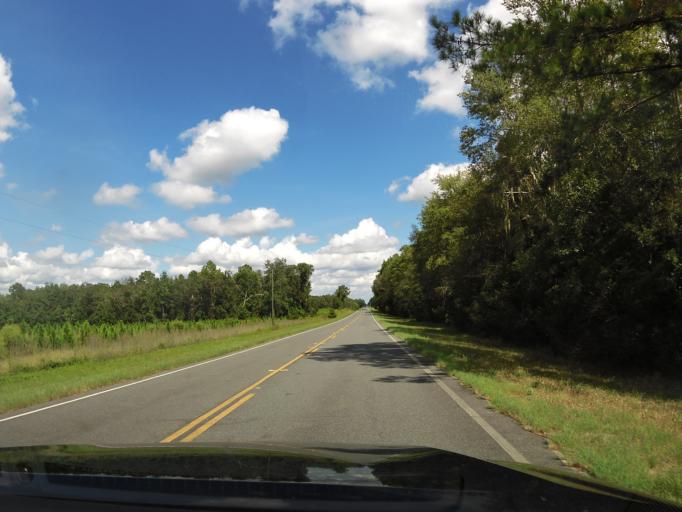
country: US
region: Florida
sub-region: Hamilton County
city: Jasper
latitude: 30.6153
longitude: -82.6321
